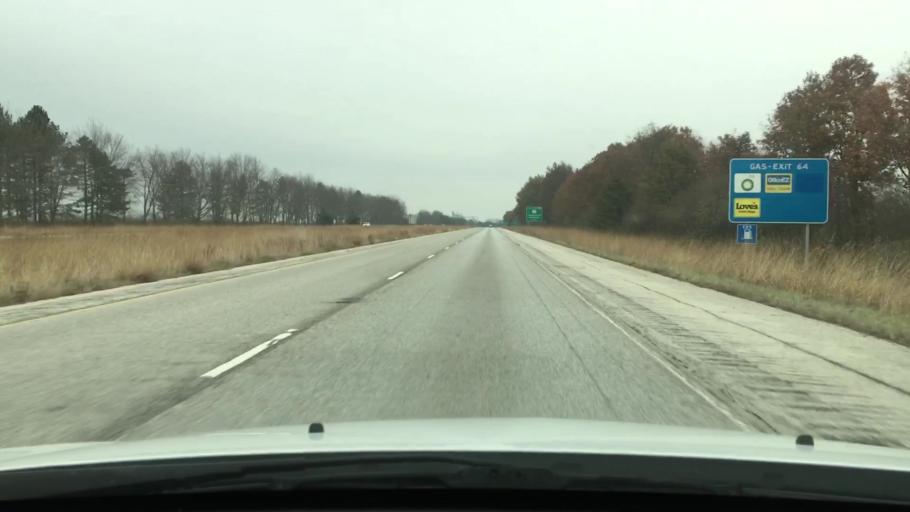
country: US
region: Illinois
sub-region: Morgan County
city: South Jacksonville
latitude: 39.6825
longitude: -90.2569
